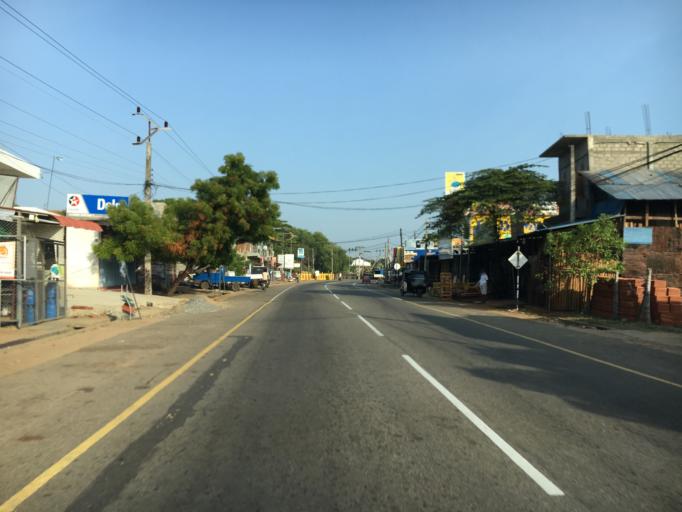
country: LK
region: Eastern Province
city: Eravur Town
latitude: 7.9096
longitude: 81.5312
